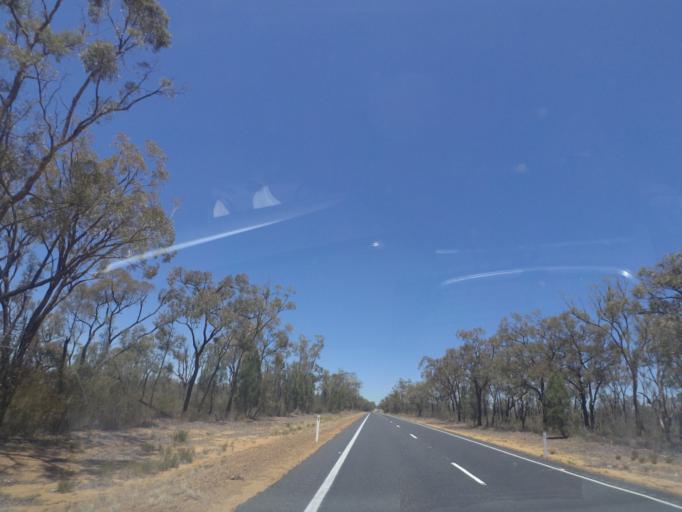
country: AU
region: New South Wales
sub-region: Narrabri
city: Narrabri
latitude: -30.7450
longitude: 149.5135
